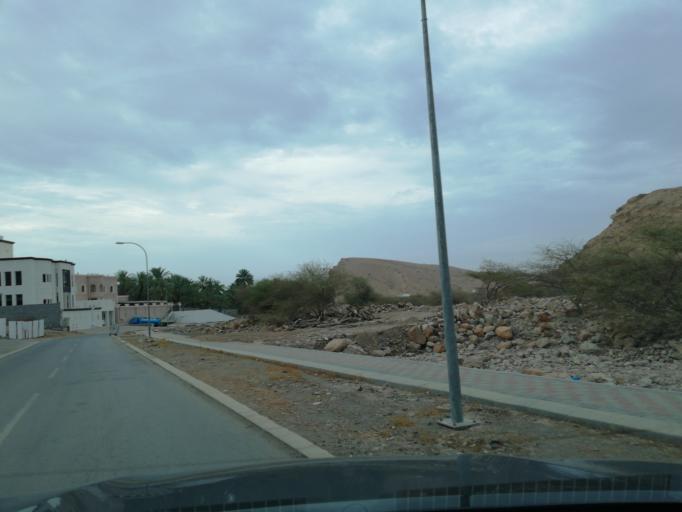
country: OM
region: Muhafazat Masqat
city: Bawshar
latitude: 23.4859
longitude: 58.3499
